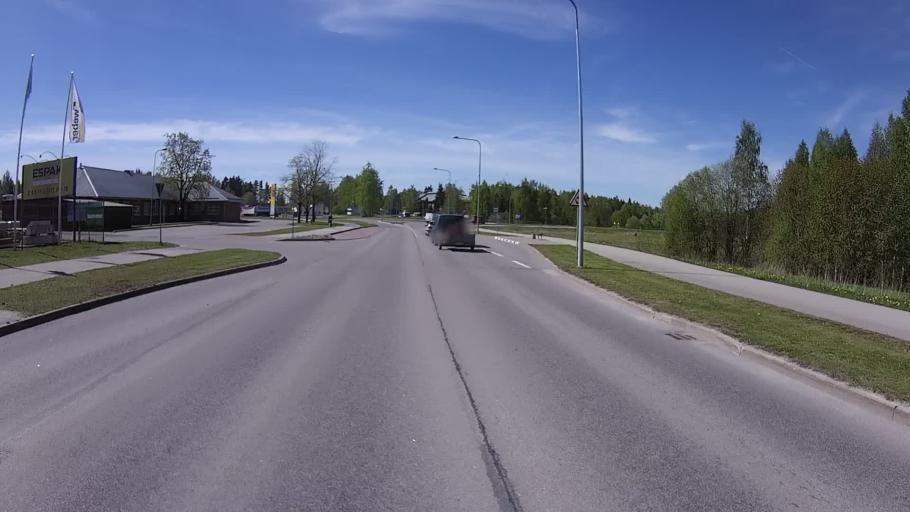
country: EE
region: Polvamaa
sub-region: Polva linn
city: Polva
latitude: 58.0680
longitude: 27.0757
